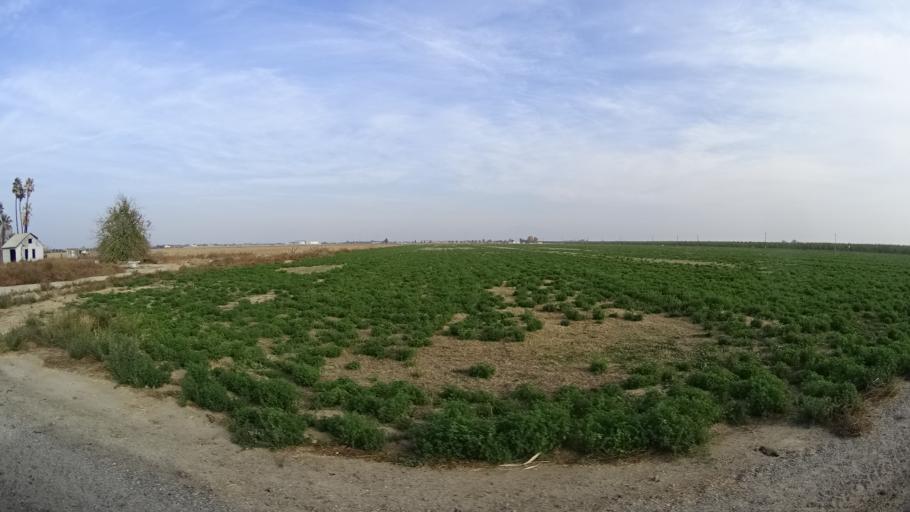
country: US
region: California
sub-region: Kern County
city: Greenacres
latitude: 35.2834
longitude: -119.1283
